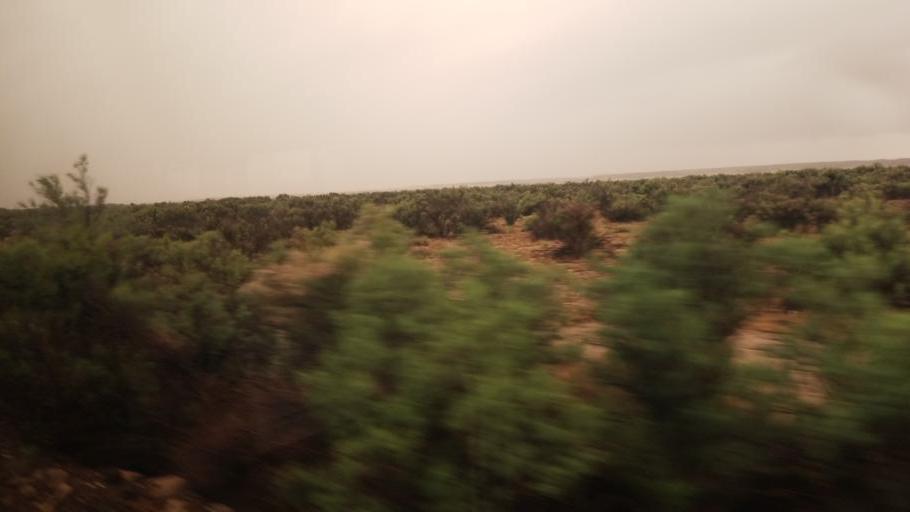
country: US
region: Arizona
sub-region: Navajo County
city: Joseph City
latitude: 34.9574
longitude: -110.3697
